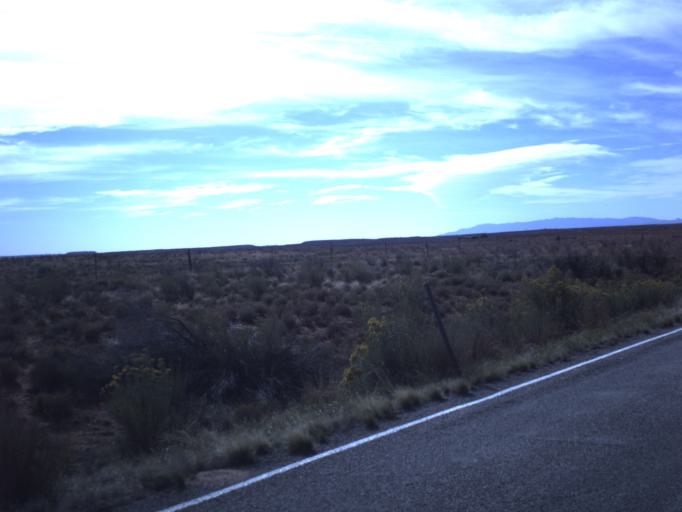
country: US
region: Utah
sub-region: San Juan County
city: Blanding
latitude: 37.3751
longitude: -109.3425
